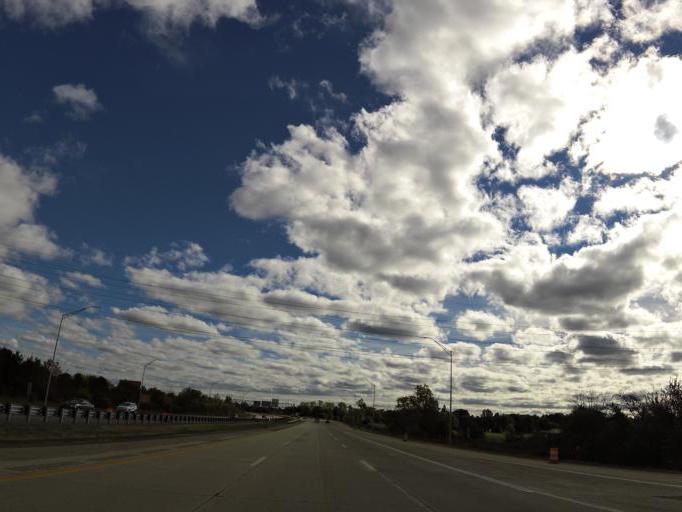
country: US
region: Michigan
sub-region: Genesee County
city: Burton
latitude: 43.0138
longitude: -83.6314
